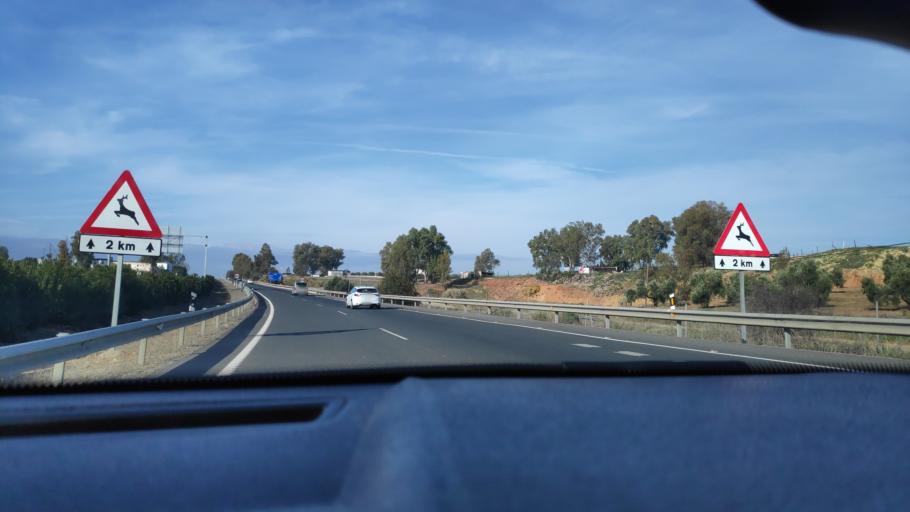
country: ES
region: Andalusia
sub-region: Provincia de Jaen
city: Linares
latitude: 38.0943
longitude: -3.6841
